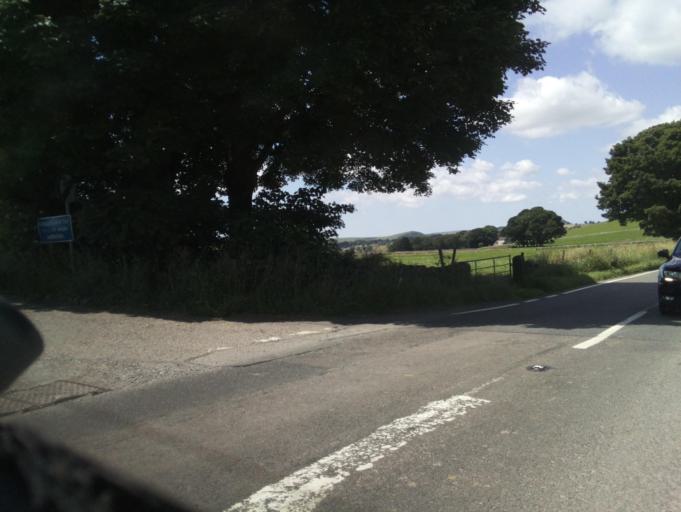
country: GB
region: England
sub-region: Derbyshire
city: Ashbourne
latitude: 53.0881
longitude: -1.7670
